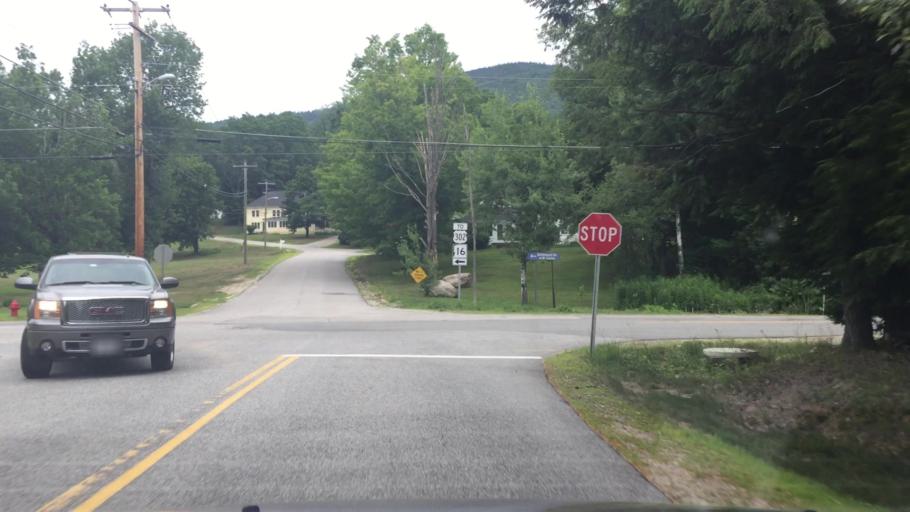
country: US
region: New Hampshire
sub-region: Carroll County
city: North Conway
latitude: 44.0750
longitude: -71.1171
